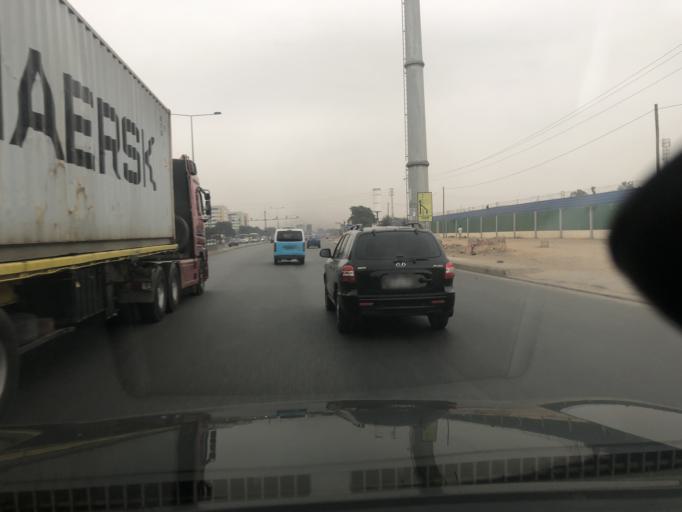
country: AO
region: Luanda
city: Luanda
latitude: -8.8507
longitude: 13.2878
